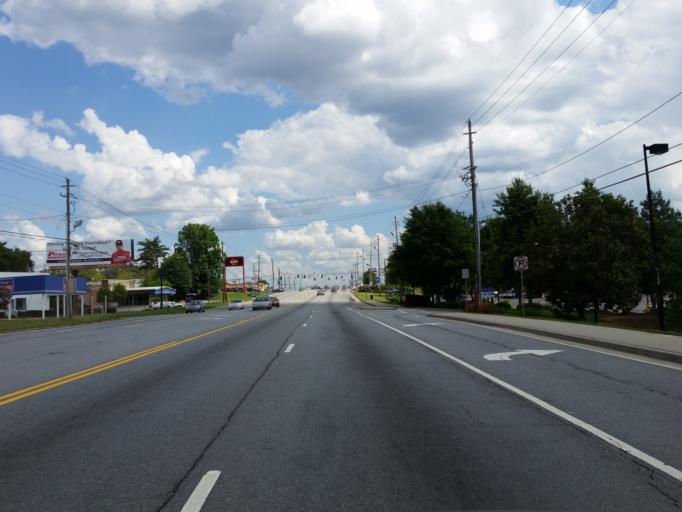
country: US
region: Georgia
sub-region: Cobb County
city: Marietta
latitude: 33.9471
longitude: -84.5187
